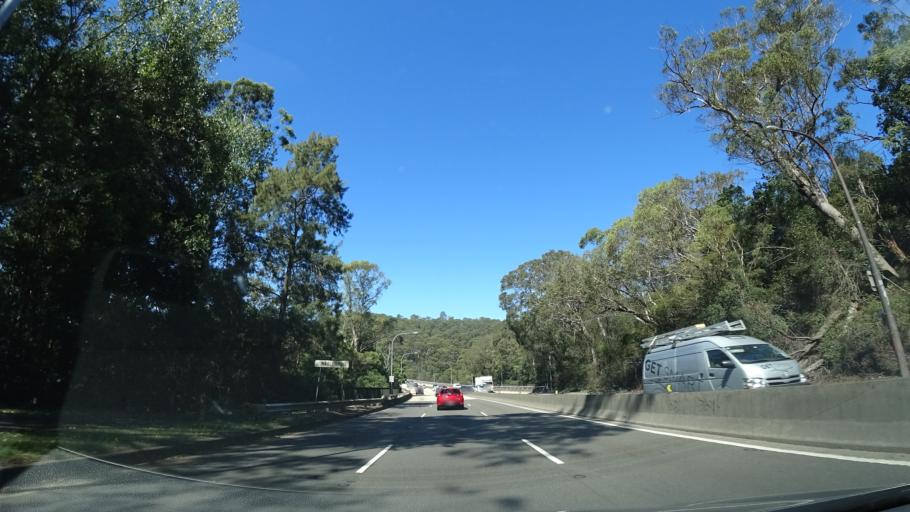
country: AU
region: New South Wales
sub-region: Ku-ring-gai
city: Roseville Chase
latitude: -33.7743
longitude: 151.2010
